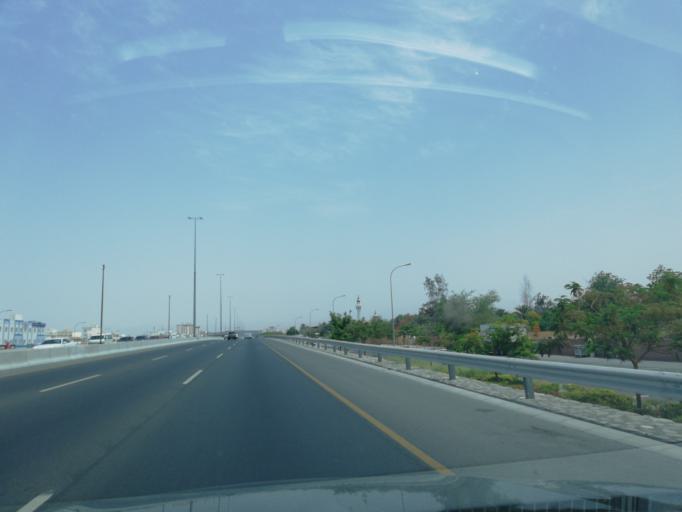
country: OM
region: Muhafazat Masqat
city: As Sib al Jadidah
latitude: 23.6364
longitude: 58.2278
